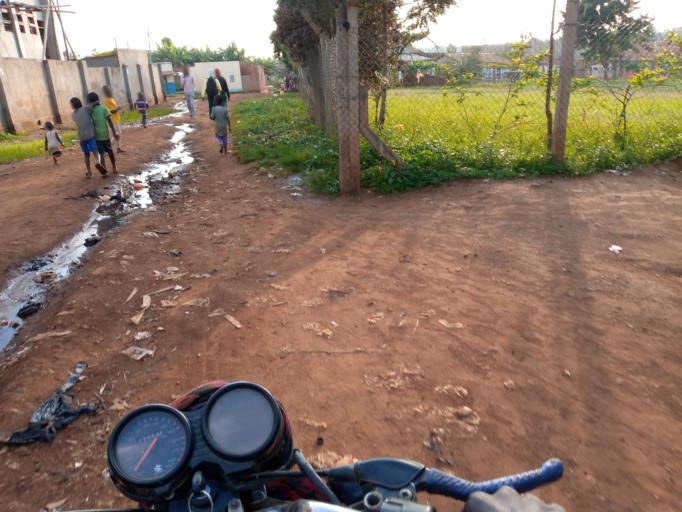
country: UG
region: Eastern Region
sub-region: Mbale District
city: Mbale
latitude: 1.0821
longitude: 34.1552
